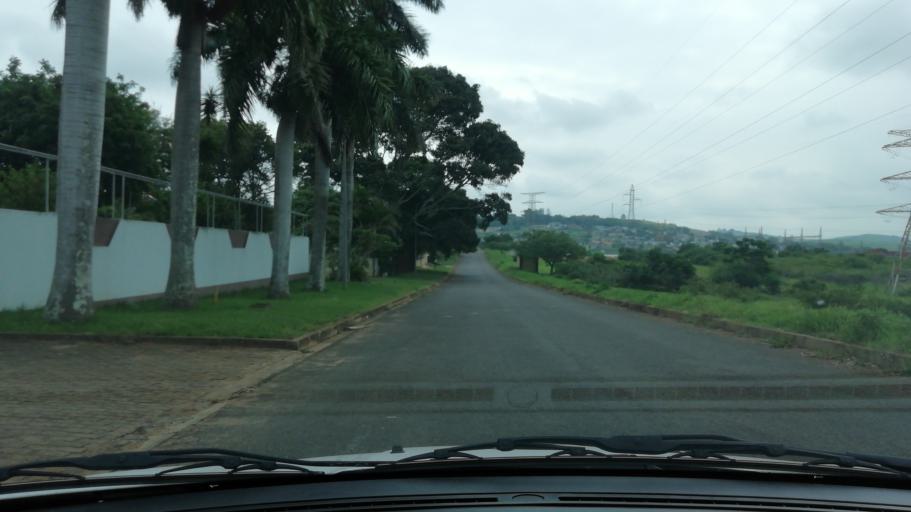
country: ZA
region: KwaZulu-Natal
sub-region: uThungulu District Municipality
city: Empangeni
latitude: -28.7372
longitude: 31.8894
